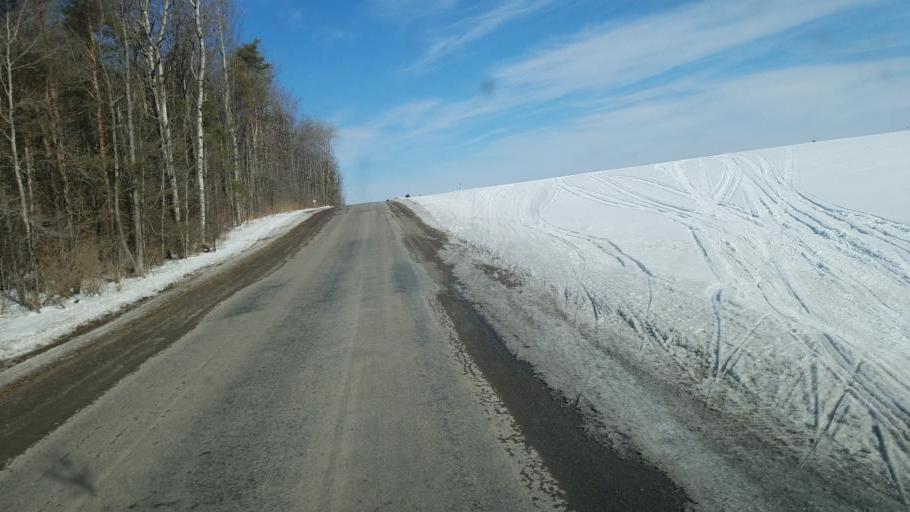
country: US
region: New York
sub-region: Allegany County
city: Andover
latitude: 42.0744
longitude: -77.7718
